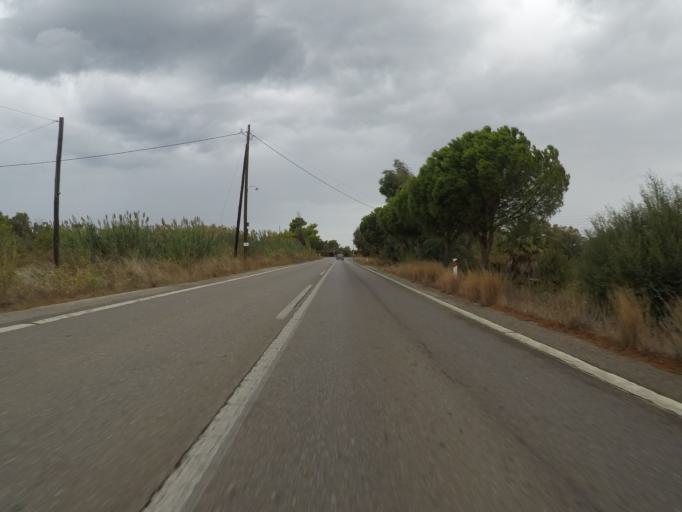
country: GR
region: West Greece
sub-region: Nomos Ileias
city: Zacharo
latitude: 37.4919
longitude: 21.6193
